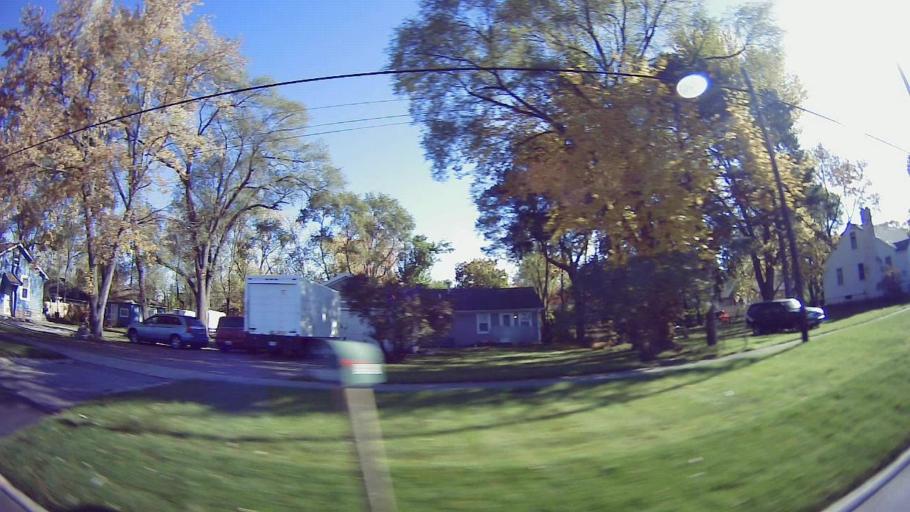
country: US
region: Michigan
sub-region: Oakland County
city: Farmington
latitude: 42.4305
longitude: -83.3750
